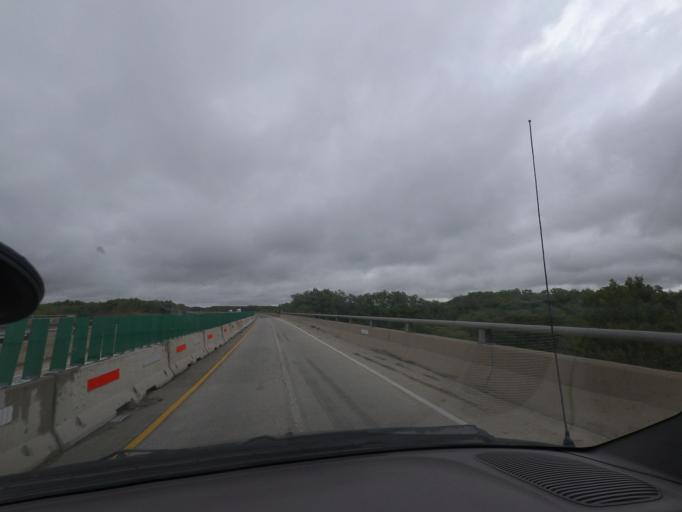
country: US
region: Illinois
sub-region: Piatt County
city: Cerro Gordo
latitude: 39.9800
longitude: -88.7962
